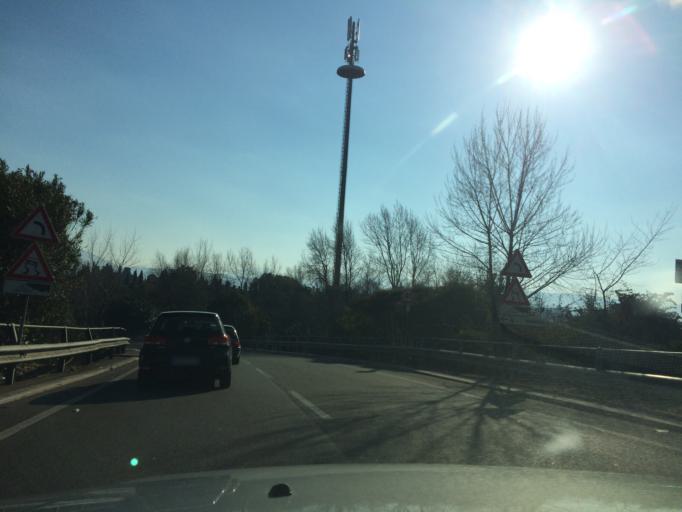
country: IT
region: Umbria
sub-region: Provincia di Terni
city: Terni
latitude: 42.5692
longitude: 12.6305
